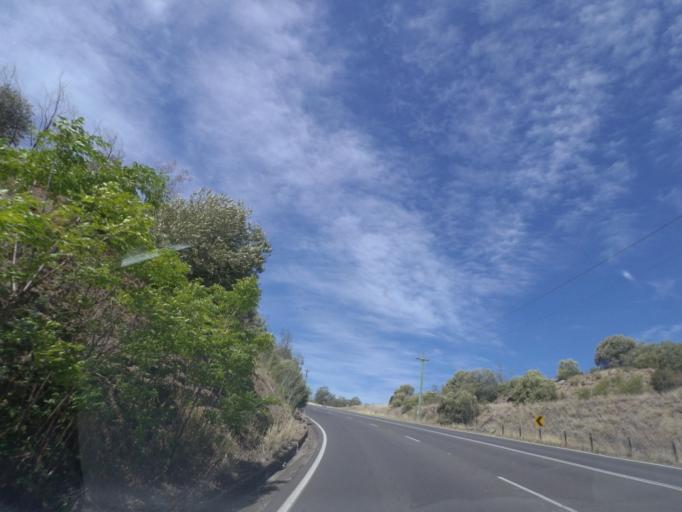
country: AU
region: New South Wales
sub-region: Wollondilly
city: Picton
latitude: -34.1544
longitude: 150.6642
